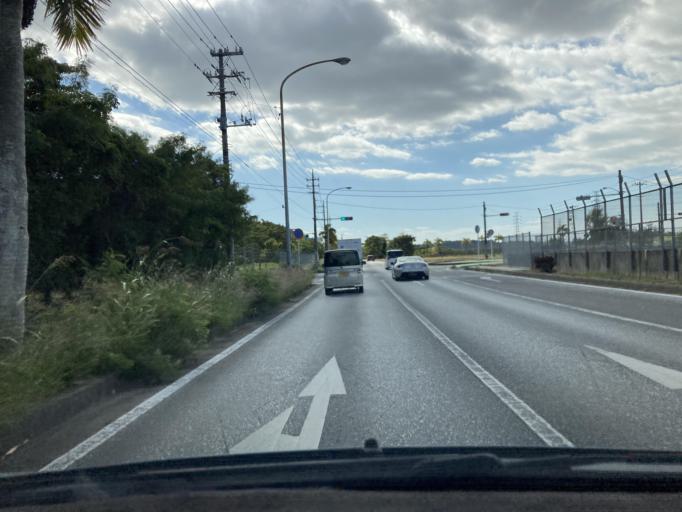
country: JP
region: Okinawa
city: Okinawa
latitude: 26.3205
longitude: 127.7897
